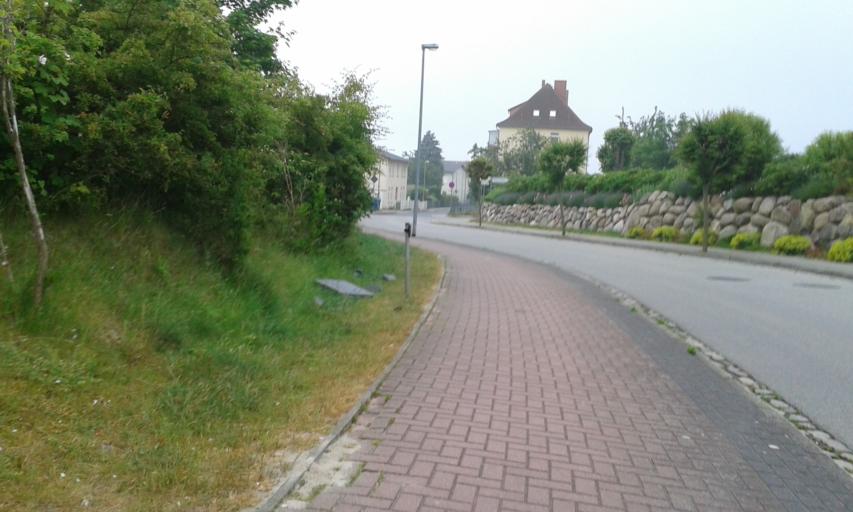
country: DE
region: Mecklenburg-Vorpommern
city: Sassnitz
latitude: 54.5177
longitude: 13.6440
